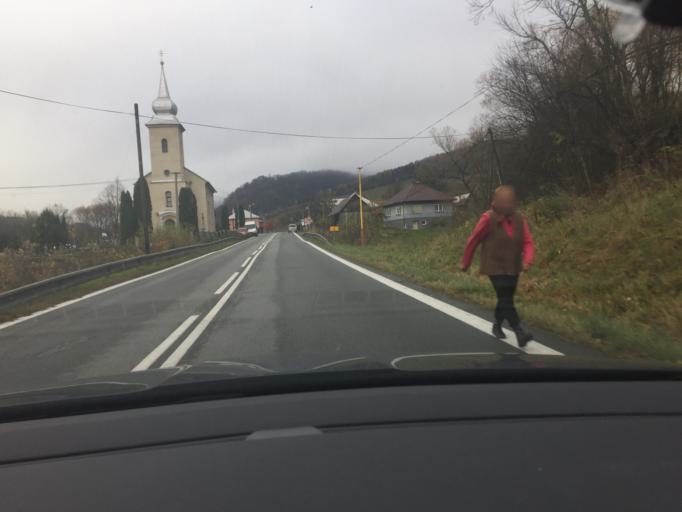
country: PL
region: Lesser Poland Voivodeship
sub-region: Powiat nowosadecki
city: Muszyna
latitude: 49.2970
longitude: 20.9346
